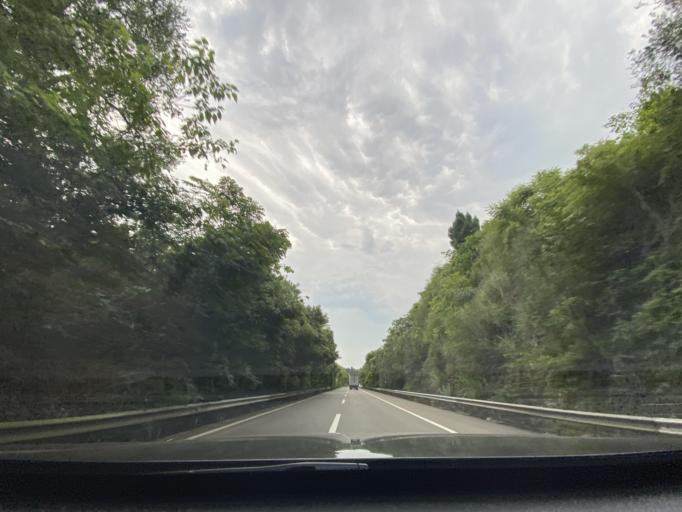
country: CN
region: Sichuan
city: Neijiang
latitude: 29.6800
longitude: 104.9586
